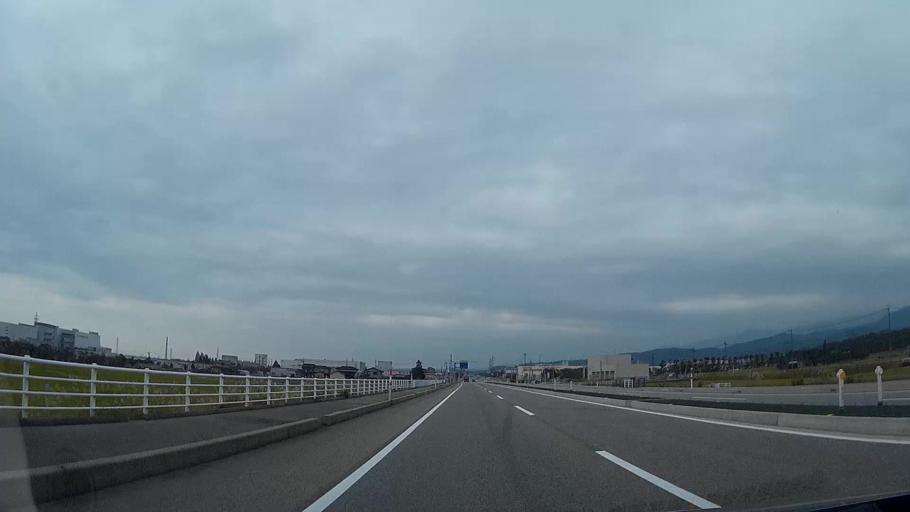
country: JP
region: Toyama
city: Uozu
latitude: 36.7747
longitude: 137.3885
